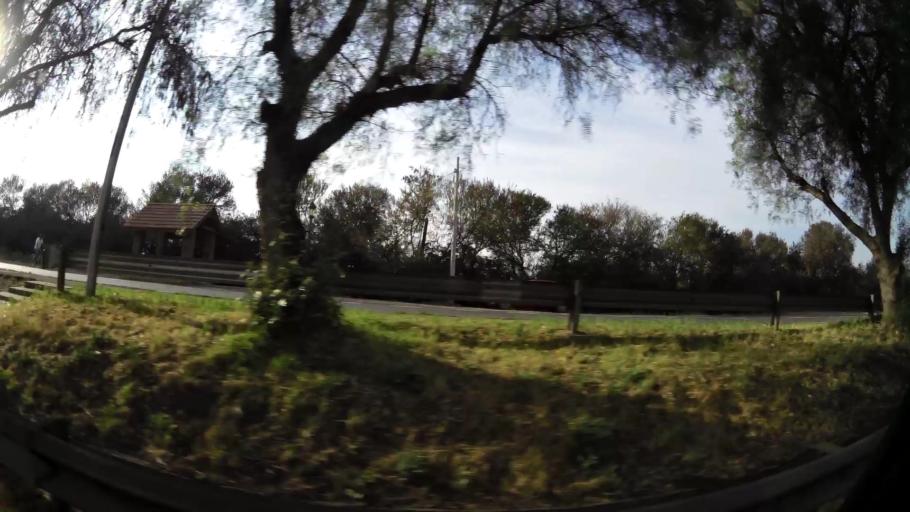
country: CL
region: Santiago Metropolitan
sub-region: Provincia de Talagante
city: Penaflor
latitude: -33.5779
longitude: -70.8243
